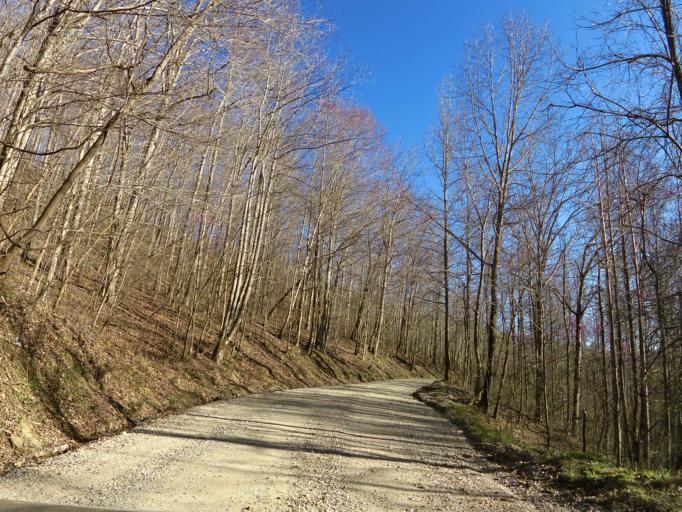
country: US
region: Tennessee
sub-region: Roane County
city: Oliver Springs
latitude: 36.2249
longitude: -84.4148
